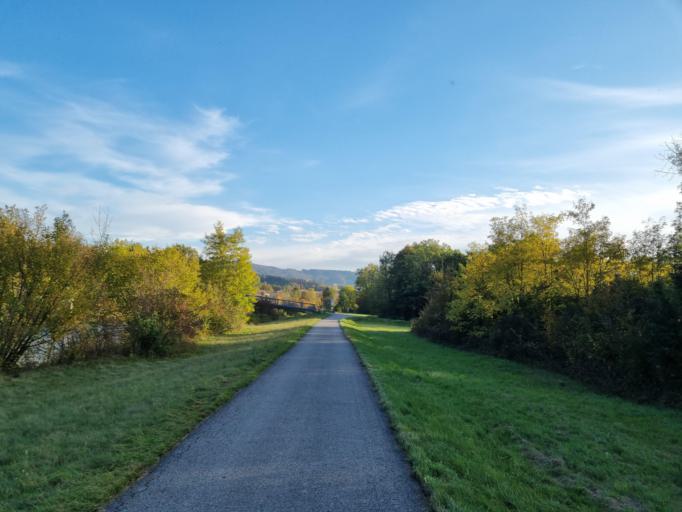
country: AT
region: Lower Austria
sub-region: Politischer Bezirk Sankt Polten
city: Pyhra
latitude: 48.1464
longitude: 15.6393
